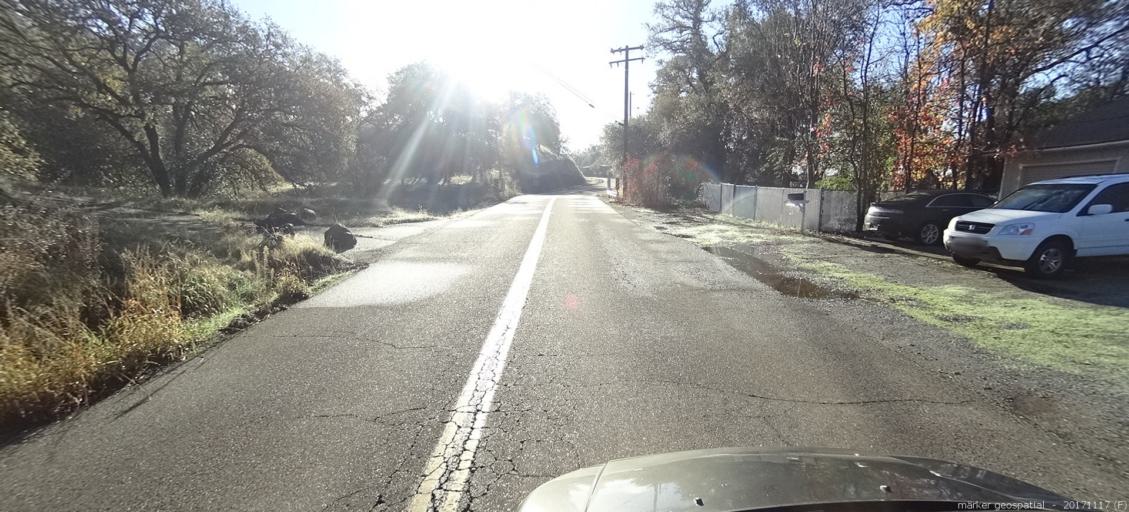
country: US
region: California
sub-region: Shasta County
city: Cottonwood
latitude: 40.4153
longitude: -122.1918
